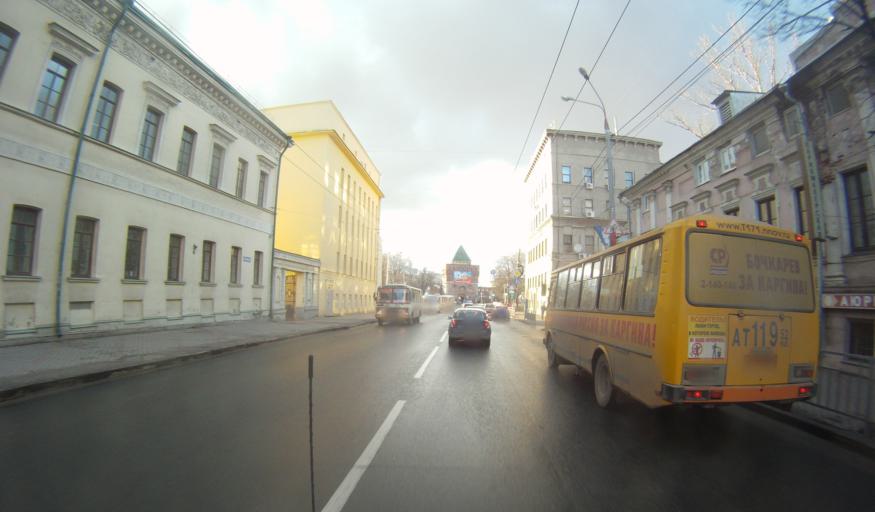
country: RU
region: Nizjnij Novgorod
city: Nizhniy Novgorod
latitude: 56.3252
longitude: 44.0078
